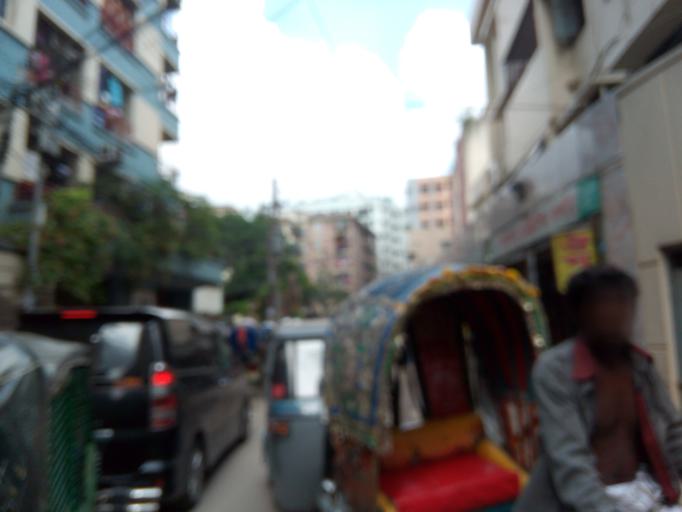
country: BD
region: Dhaka
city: Azimpur
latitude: 23.7418
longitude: 90.3876
